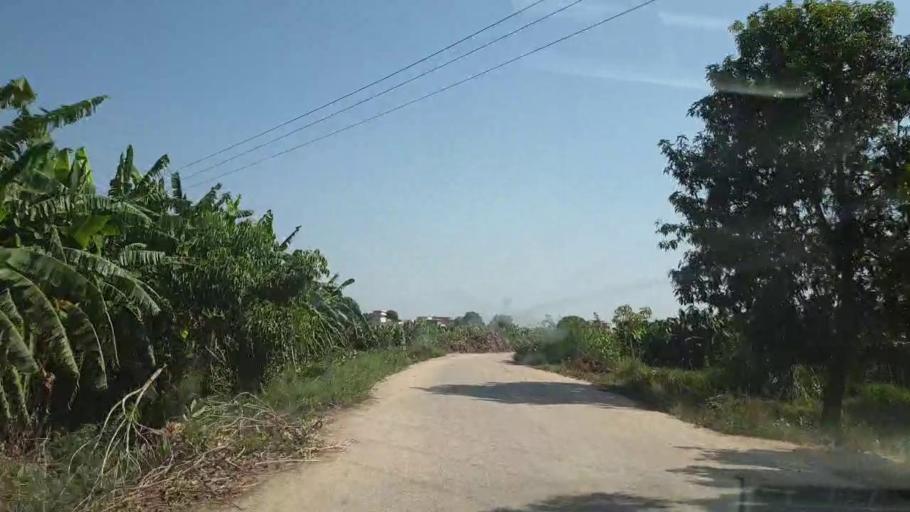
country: PK
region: Sindh
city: Tando Jam
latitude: 25.4024
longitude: 68.5855
